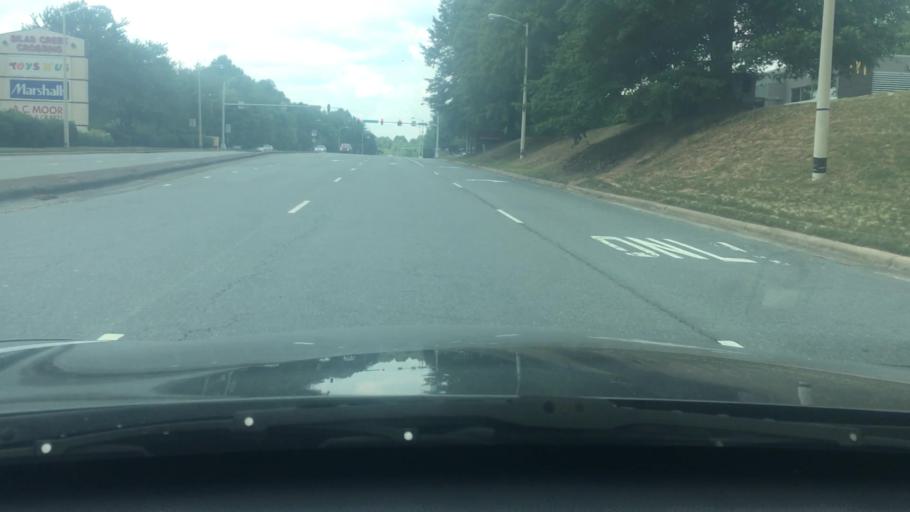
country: US
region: North Carolina
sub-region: Forsyth County
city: Winston-Salem
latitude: 36.0711
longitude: -80.2971
